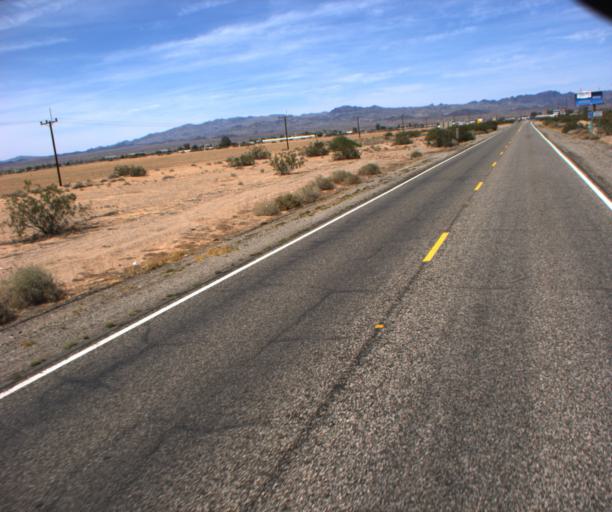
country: US
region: Arizona
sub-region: La Paz County
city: Parker
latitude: 34.1234
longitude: -114.2792
